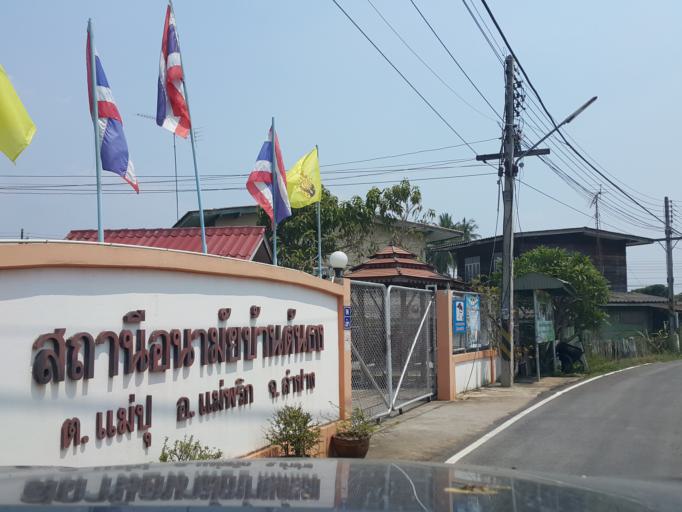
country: TH
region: Lampang
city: Mae Phrik
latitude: 17.5152
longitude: 99.1464
